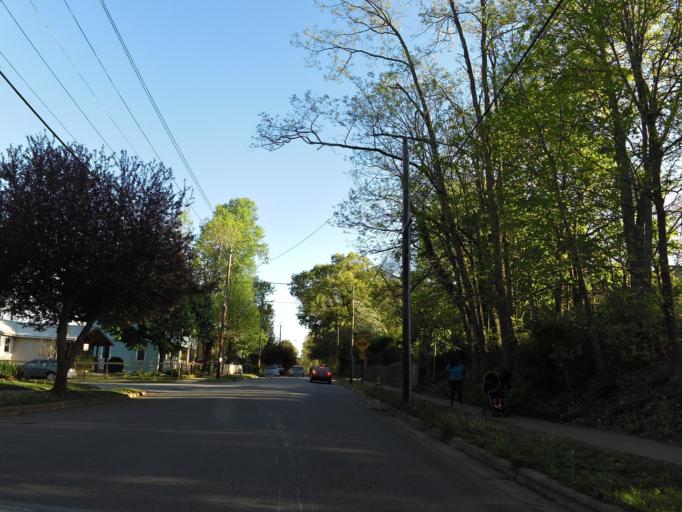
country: US
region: North Carolina
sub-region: Buncombe County
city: Asheville
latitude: 35.5900
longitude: -82.5591
